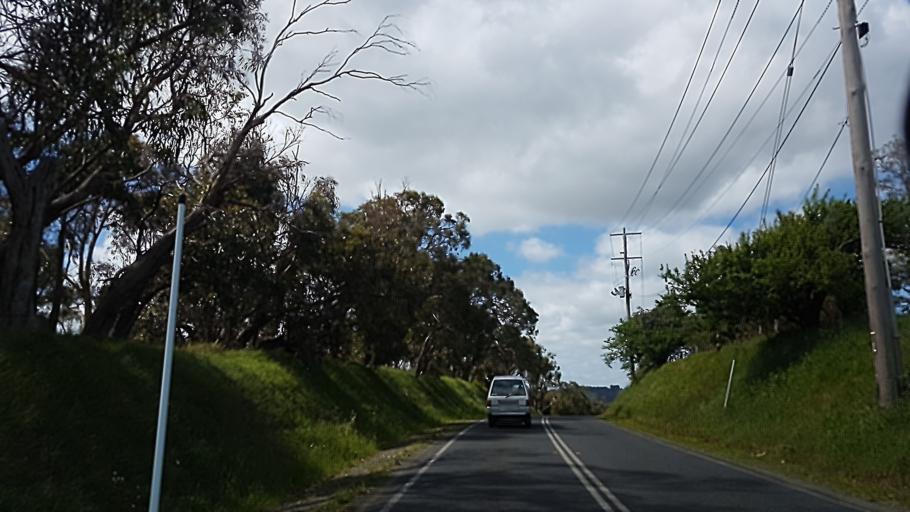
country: AU
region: Victoria
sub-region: Yarra Ranges
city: Tremont
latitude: -37.9107
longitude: 145.3123
